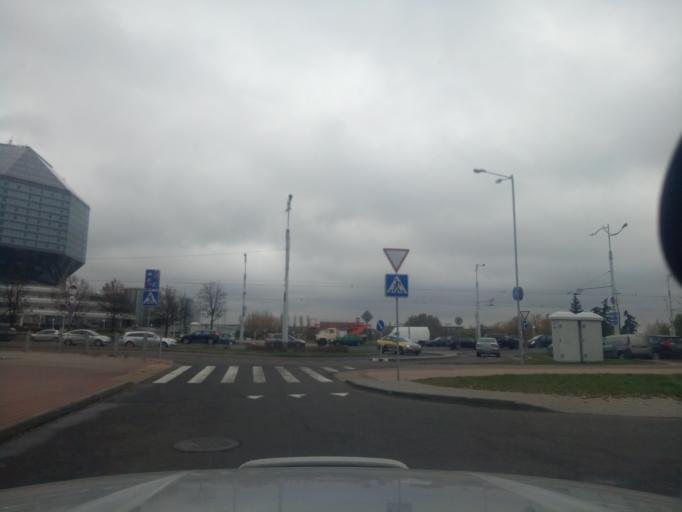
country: BY
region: Minsk
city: Borovlyany
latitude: 53.9328
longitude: 27.6432
